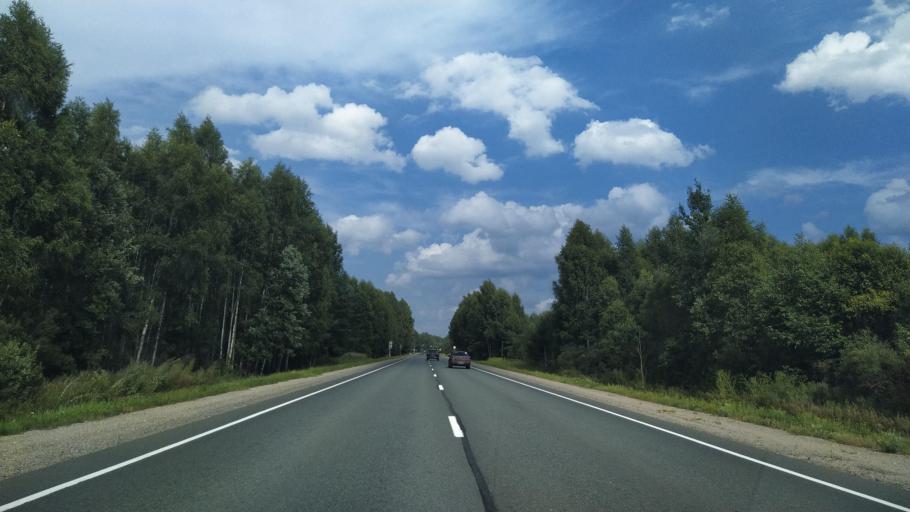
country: RU
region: Pskov
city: Porkhov
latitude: 57.8592
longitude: 29.5663
